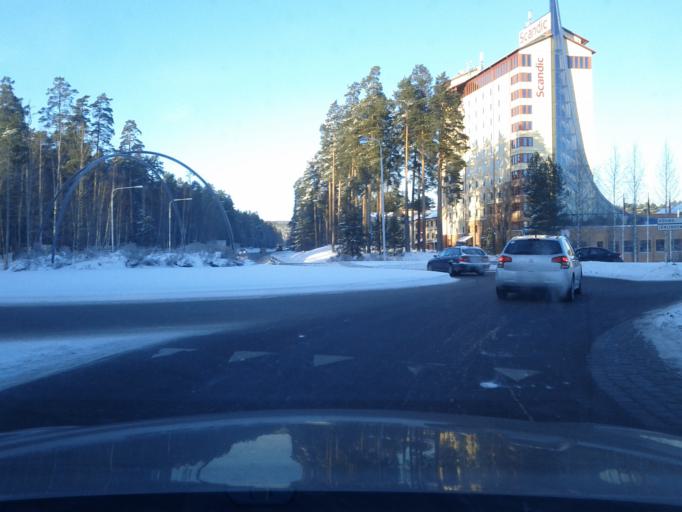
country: SE
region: Dalarna
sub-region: Faluns Kommun
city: Falun
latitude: 60.6119
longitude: 15.6526
